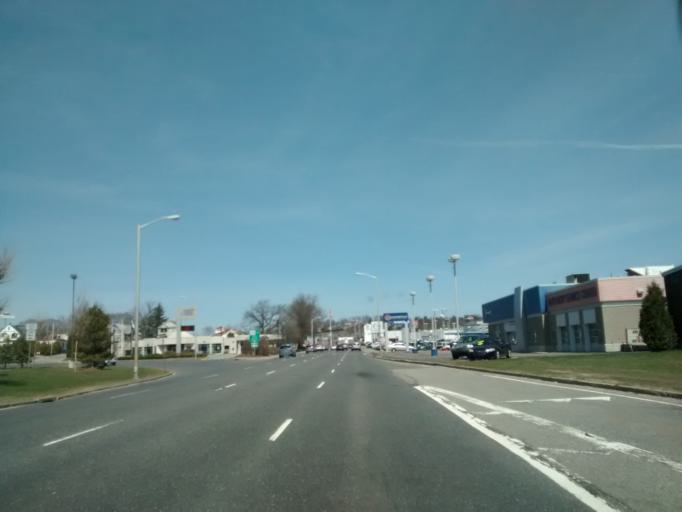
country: US
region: Massachusetts
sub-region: Worcester County
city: Worcester
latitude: 42.2876
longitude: -71.8056
